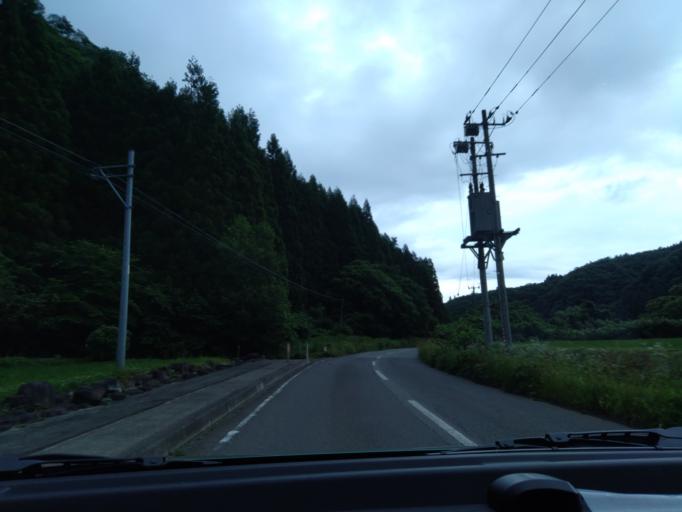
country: JP
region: Iwate
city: Ichinoseki
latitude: 38.8243
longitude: 140.9132
